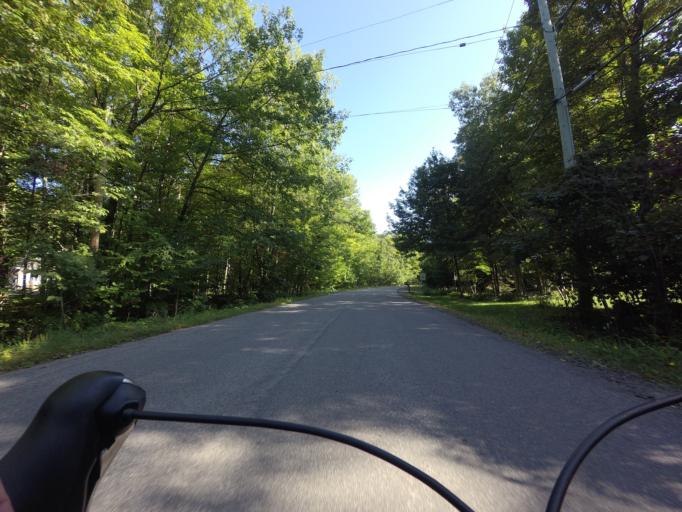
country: CA
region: Ontario
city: Bells Corners
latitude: 45.4876
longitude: -76.0482
